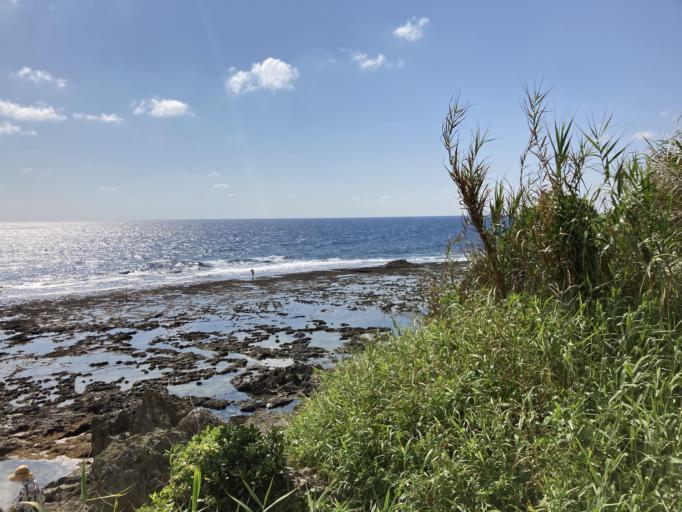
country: JP
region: Okinawa
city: Itoman
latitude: 26.1007
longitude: 127.7346
